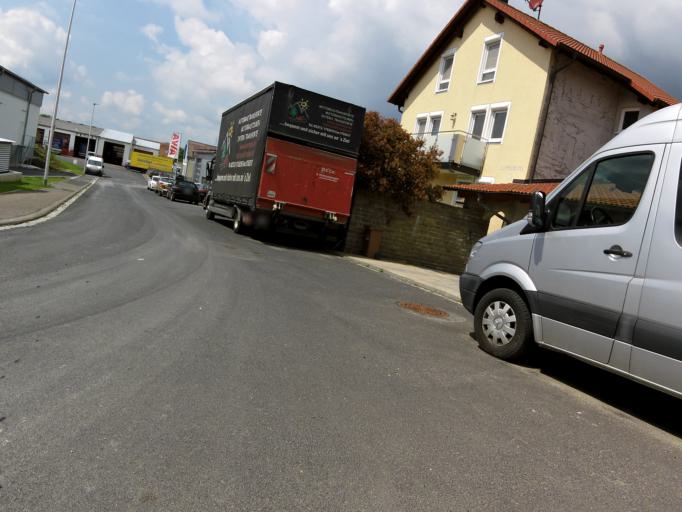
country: DE
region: Bavaria
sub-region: Regierungsbezirk Unterfranken
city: Waldbuttelbrunn
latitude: 49.7872
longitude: 9.8337
